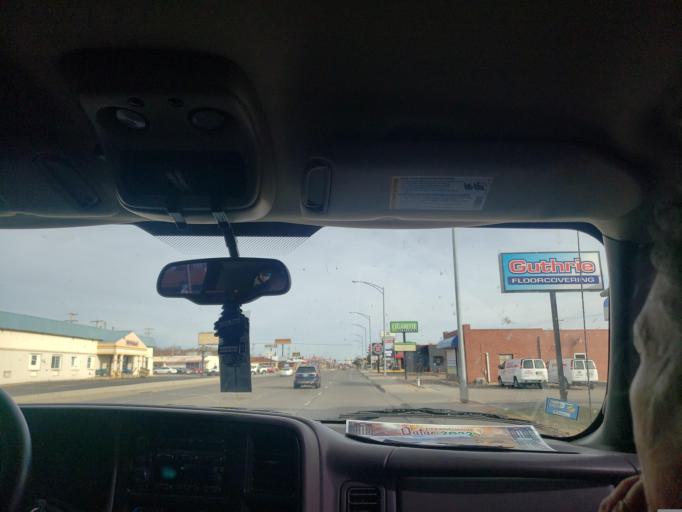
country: US
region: Kansas
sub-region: Ford County
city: Dodge City
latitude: 37.7539
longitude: -100.0365
